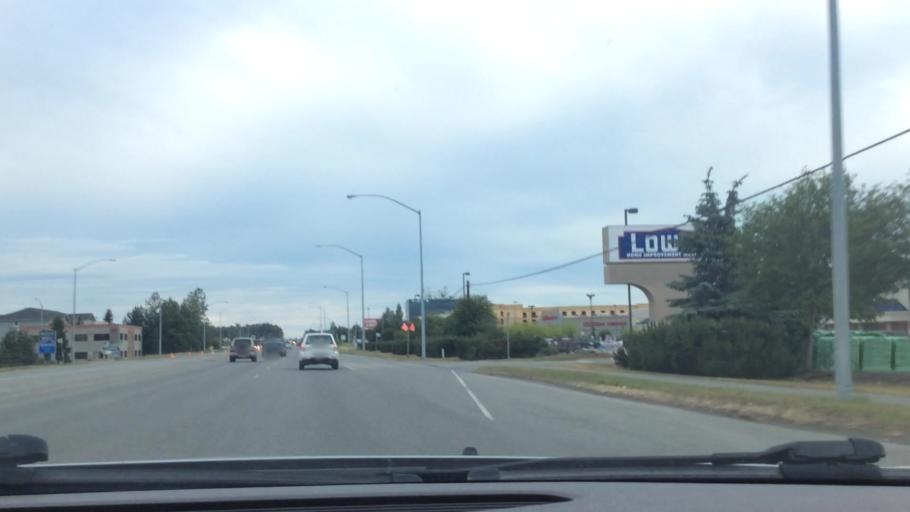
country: US
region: Alaska
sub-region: Anchorage Municipality
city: Anchorage
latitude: 61.1792
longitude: -149.8764
